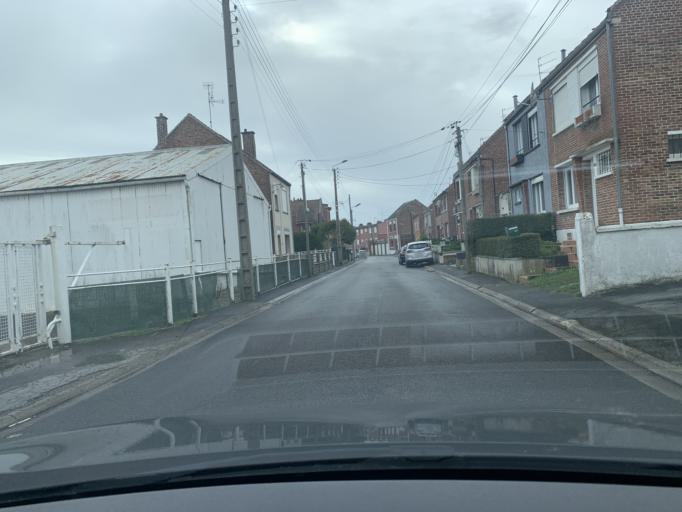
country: FR
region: Nord-Pas-de-Calais
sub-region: Departement du Nord
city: Neuville-Saint-Remy
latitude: 50.1812
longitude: 3.2151
